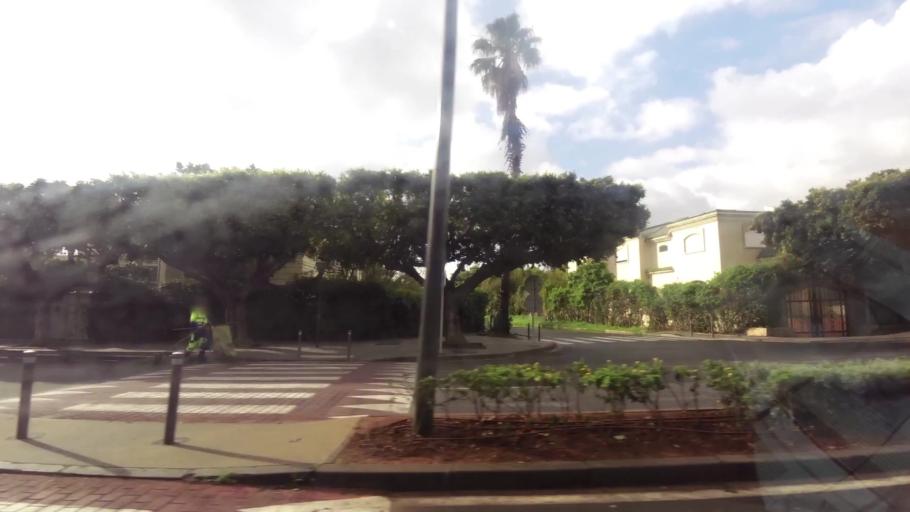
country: MA
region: Grand Casablanca
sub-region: Casablanca
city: Casablanca
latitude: 33.5832
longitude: -7.6594
